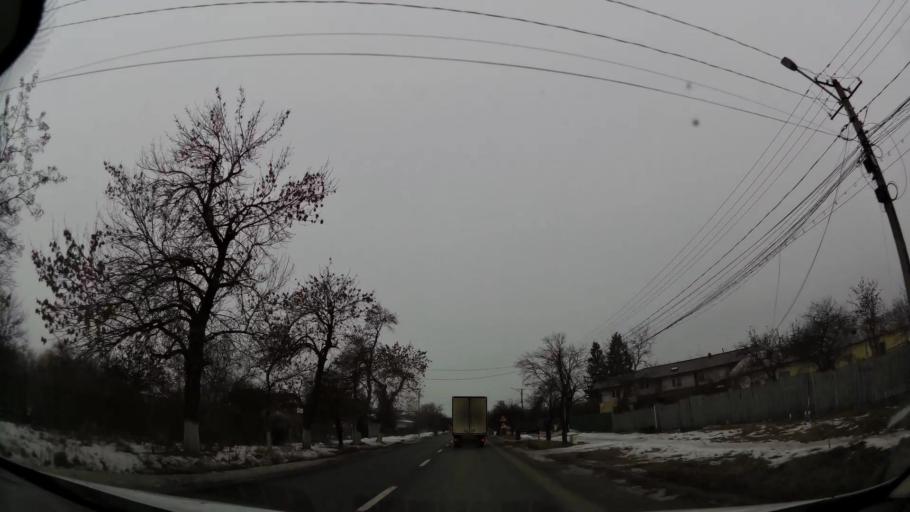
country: RO
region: Dambovita
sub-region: Comuna Tartasesti
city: Baldana
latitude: 44.6033
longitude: 25.7738
